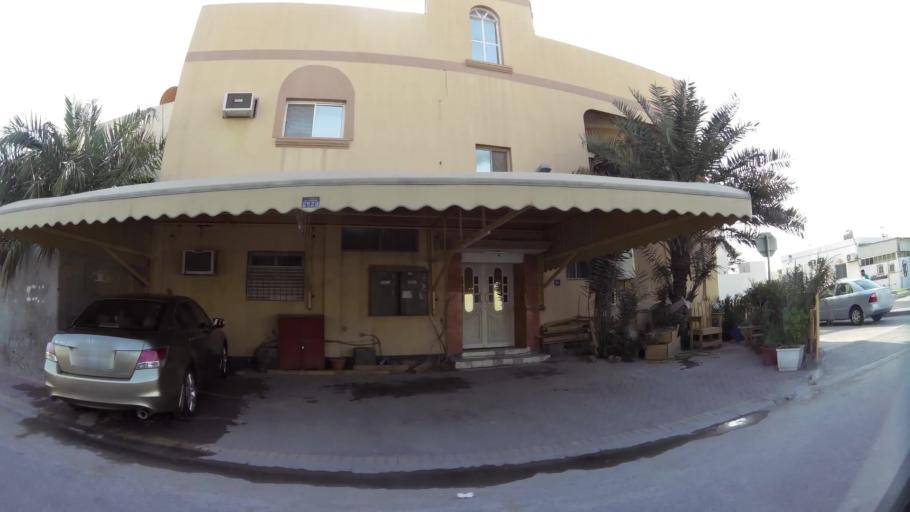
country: BH
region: Manama
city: Jidd Hafs
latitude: 26.2127
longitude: 50.5132
